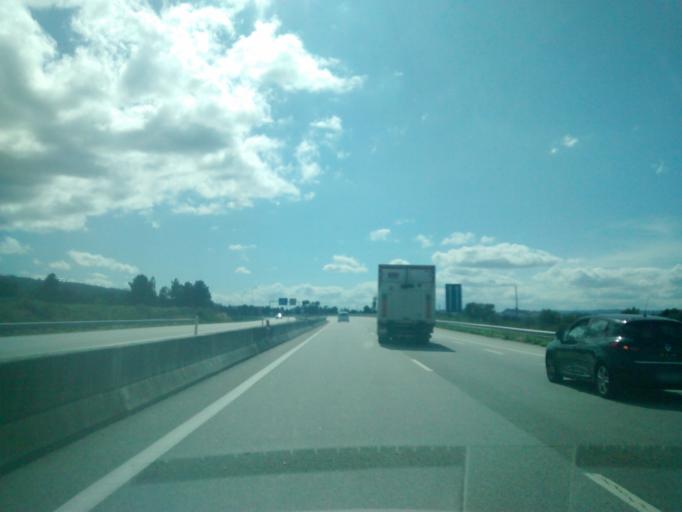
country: PT
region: Guarda
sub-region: Celorico da Beira
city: Celorico da Beira
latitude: 40.6401
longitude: -7.3443
